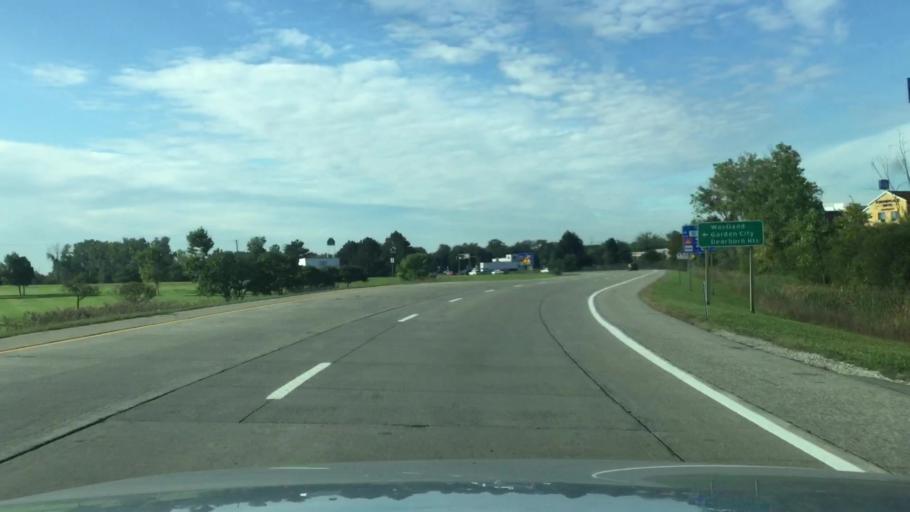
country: US
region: Michigan
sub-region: Wayne County
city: Canton
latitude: 42.3260
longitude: -83.4443
